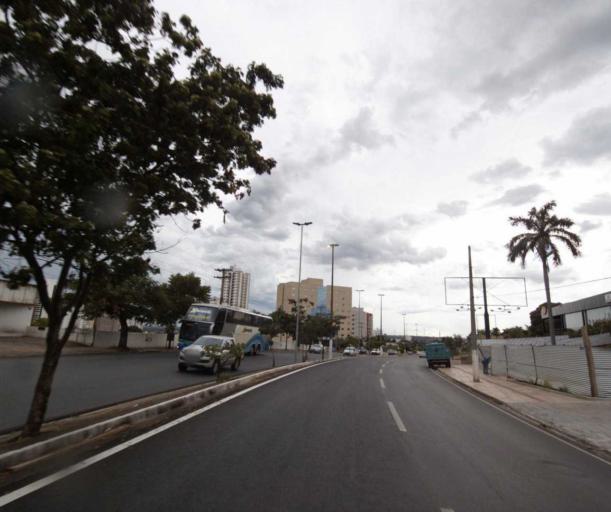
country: BR
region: Mato Grosso
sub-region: Cuiaba
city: Cuiaba
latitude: -15.6031
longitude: -56.0764
